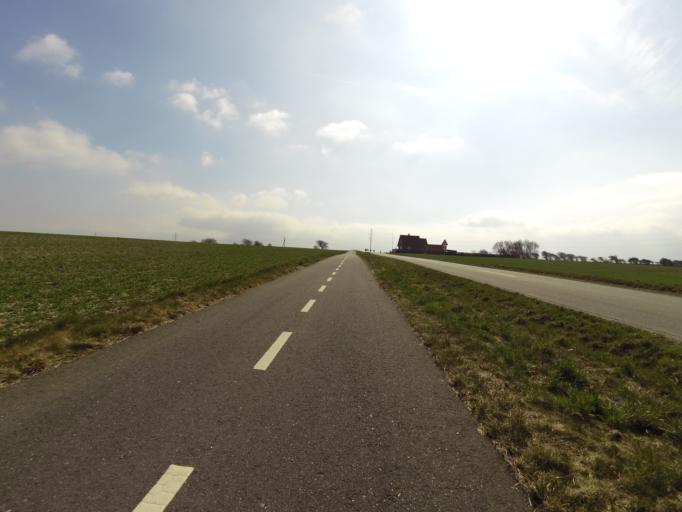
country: DK
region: Central Jutland
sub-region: Struer Kommune
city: Struer
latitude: 56.4618
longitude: 8.6115
